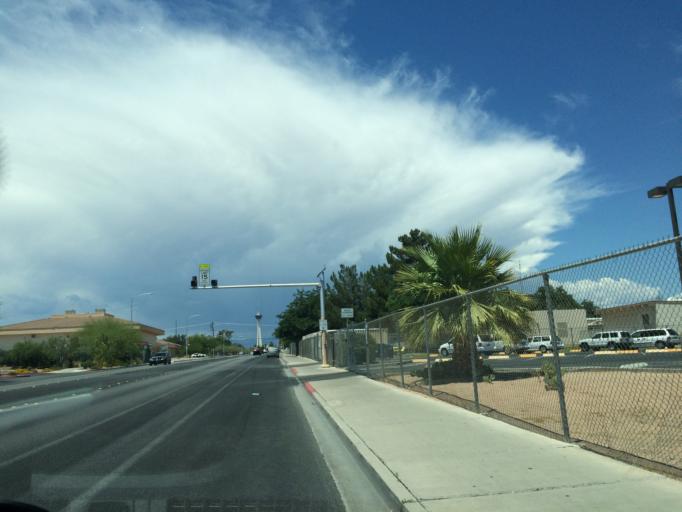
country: US
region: Nevada
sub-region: Clark County
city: Winchester
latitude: 36.1482
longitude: -115.1122
